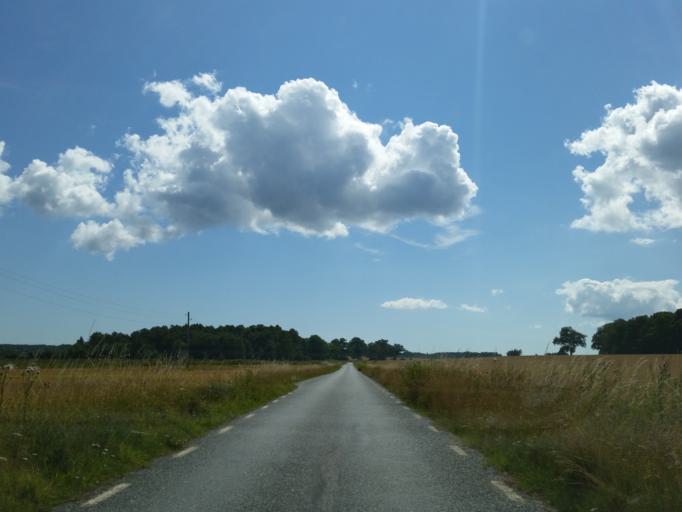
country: SE
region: Stockholm
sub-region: Sodertalje Kommun
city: Pershagen
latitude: 59.0482
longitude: 17.6592
